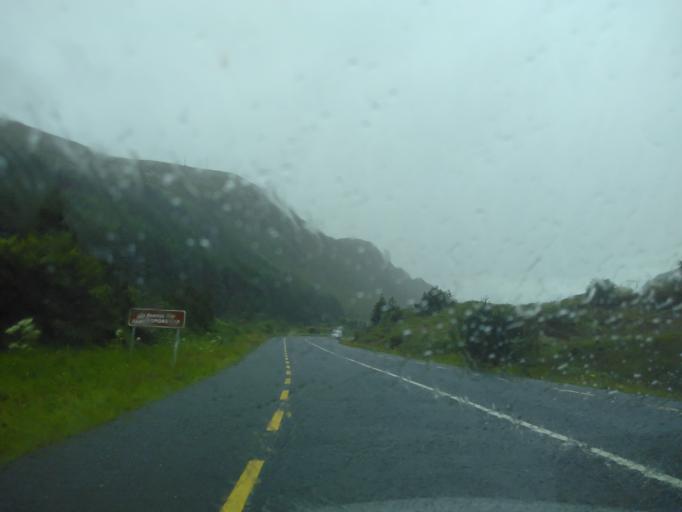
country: IE
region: Ulster
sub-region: County Donegal
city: Ballybofey
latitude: 54.7298
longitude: -7.9408
